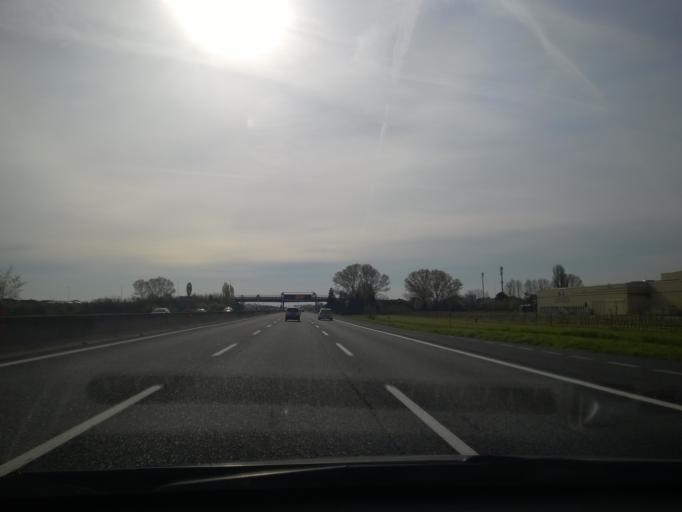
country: IT
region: Emilia-Romagna
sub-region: Forli-Cesena
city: Forli
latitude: 44.2579
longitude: 12.0760
